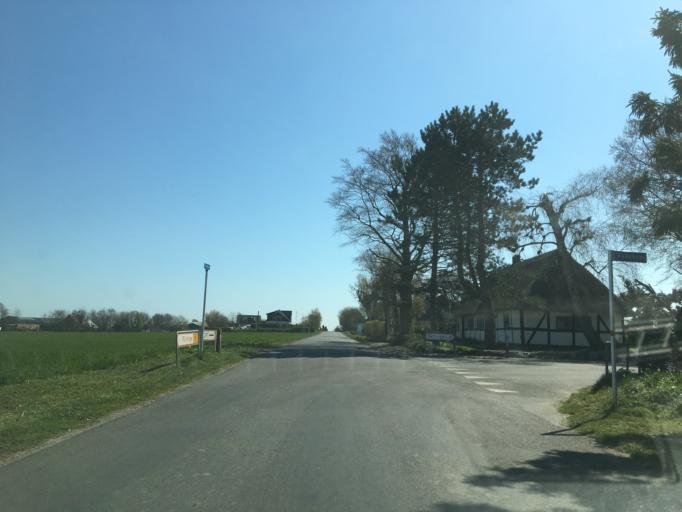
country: DK
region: Zealand
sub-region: Guldborgsund Kommune
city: Nykobing Falster
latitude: 54.7421
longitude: 11.7867
